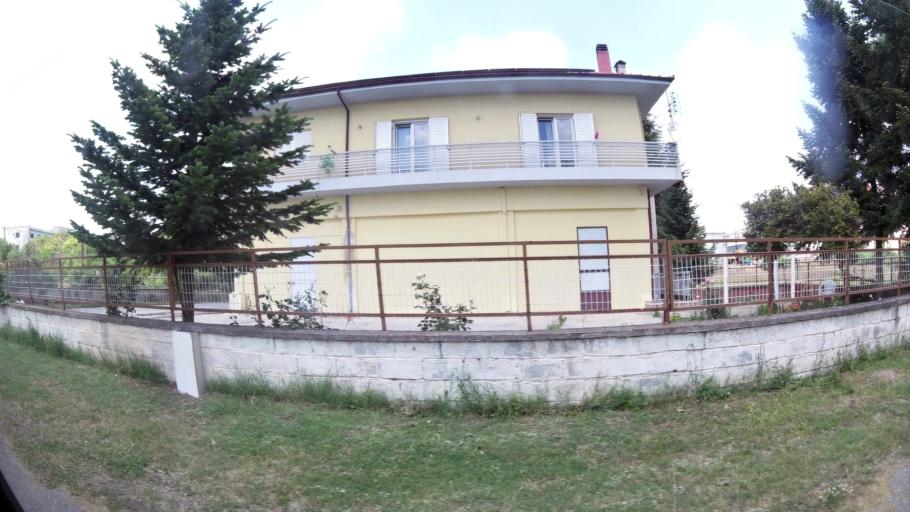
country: GR
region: West Macedonia
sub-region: Nomos Kozanis
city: Kozani
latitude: 40.2869
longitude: 21.7810
